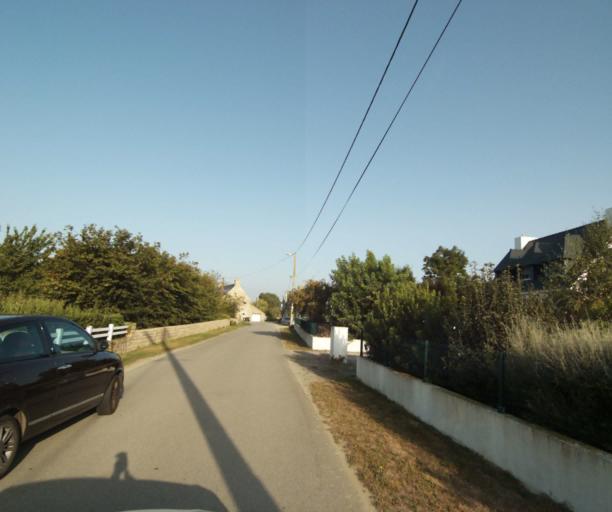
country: FR
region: Brittany
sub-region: Departement du Morbihan
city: Riantec
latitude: 47.7044
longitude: -3.2979
